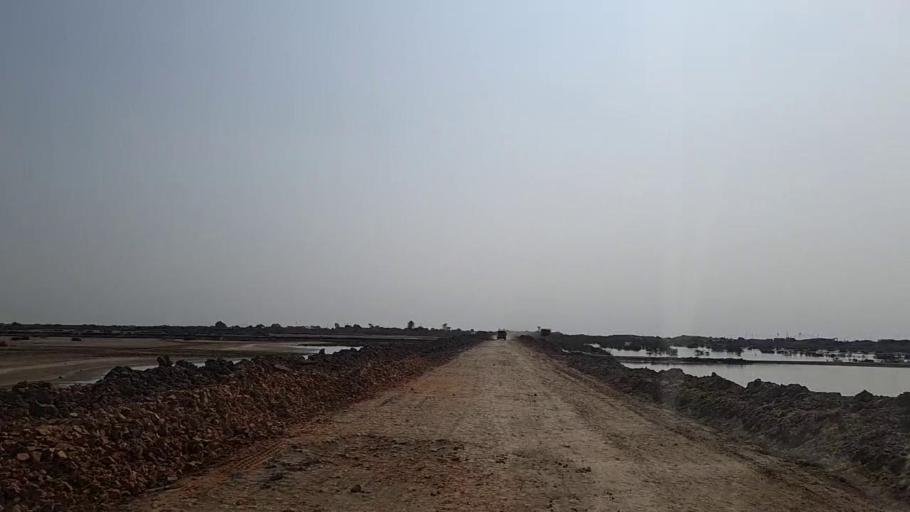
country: PK
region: Sindh
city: Chuhar Jamali
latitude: 24.1959
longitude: 67.8484
